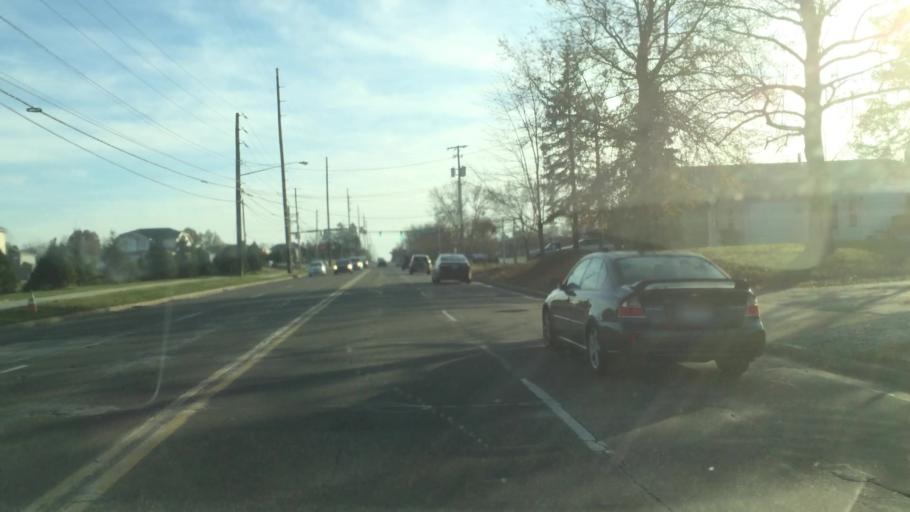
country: US
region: Ohio
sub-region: Summit County
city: Stow
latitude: 41.1921
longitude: -81.4405
